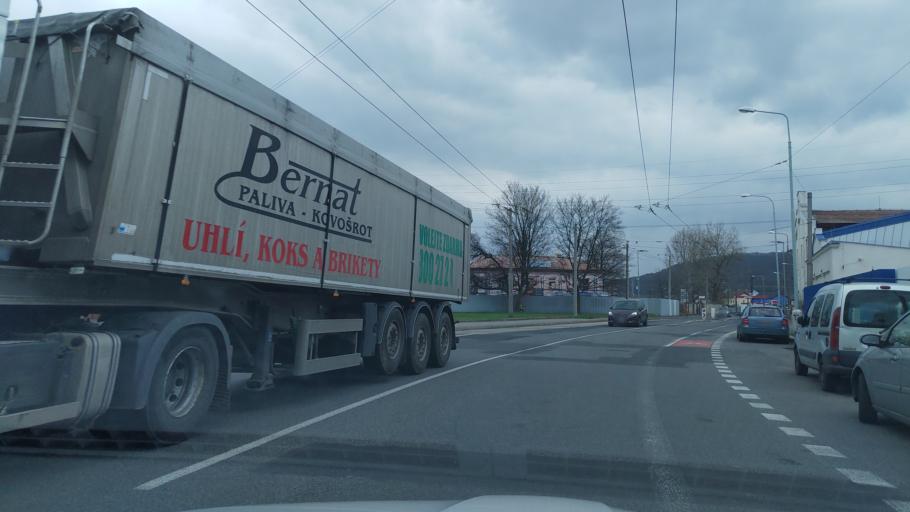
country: CZ
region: Ustecky
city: Trmice
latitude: 50.6569
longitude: 14.0071
